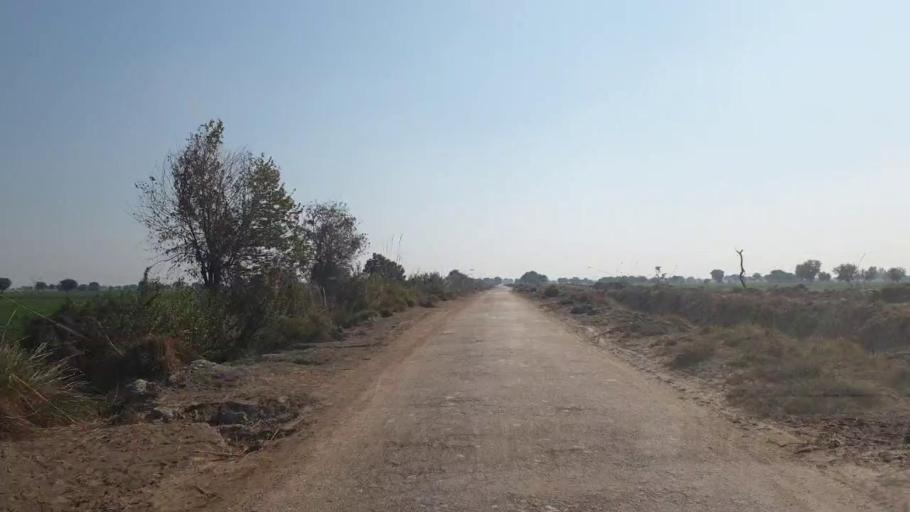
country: PK
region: Sindh
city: Shahdadpur
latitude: 25.9545
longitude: 68.6283
